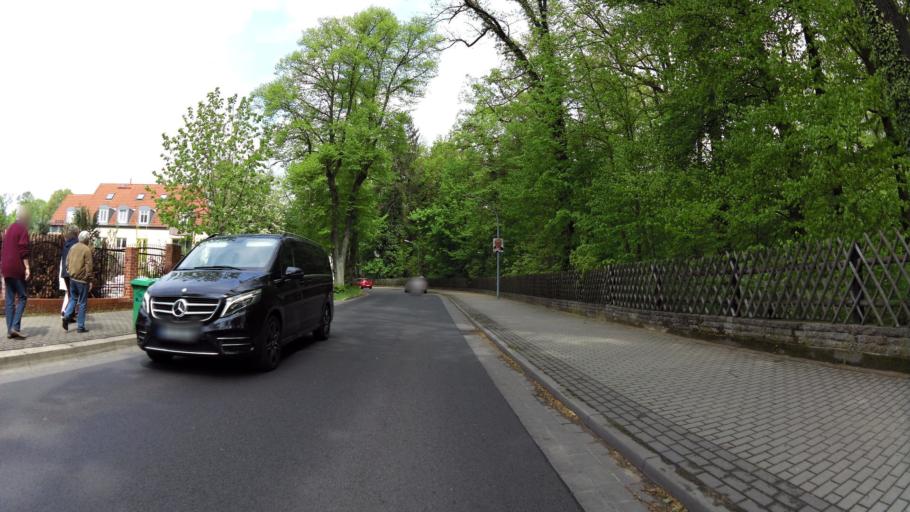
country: DE
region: Brandenburg
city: Konigs Wusterhausen
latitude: 52.2950
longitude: 13.6495
